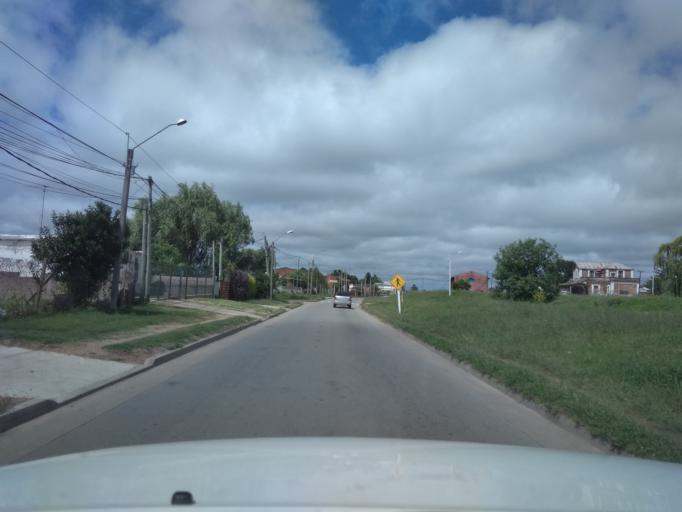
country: UY
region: Canelones
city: Pando
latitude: -34.7163
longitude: -55.9651
